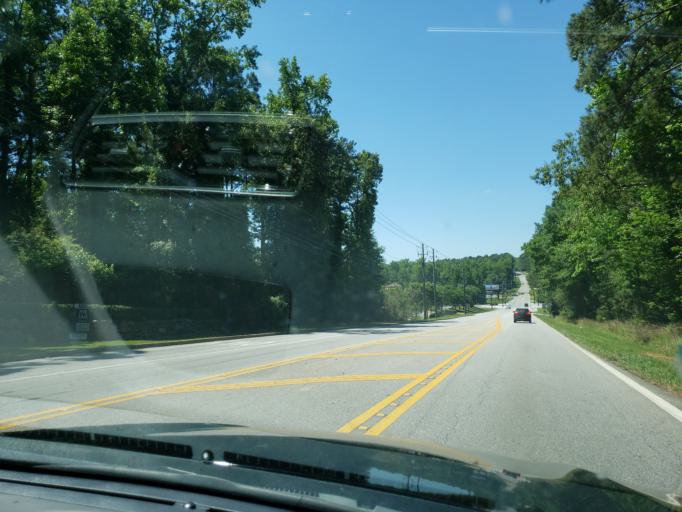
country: US
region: Alabama
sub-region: Lee County
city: Auburn
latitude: 32.6395
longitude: -85.4816
